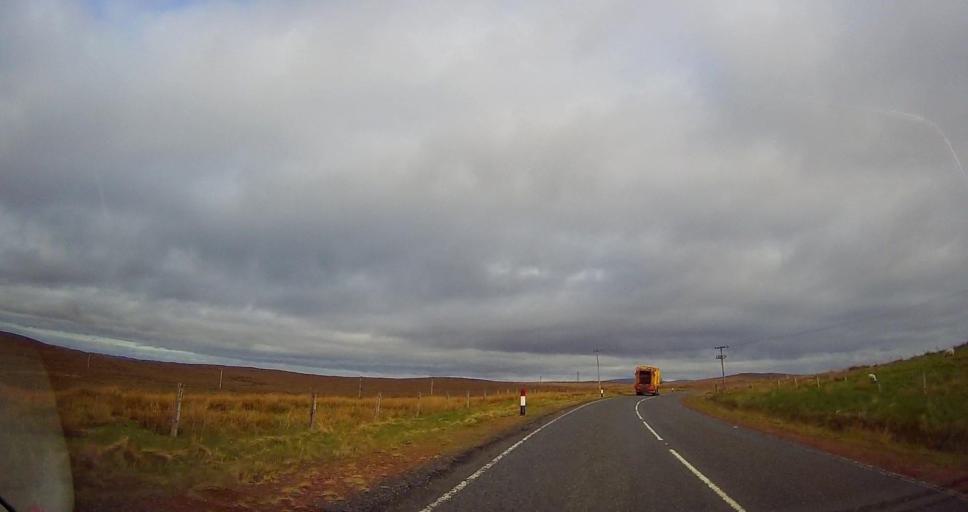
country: GB
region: Scotland
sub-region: Shetland Islands
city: Lerwick
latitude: 60.4471
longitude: -1.2081
